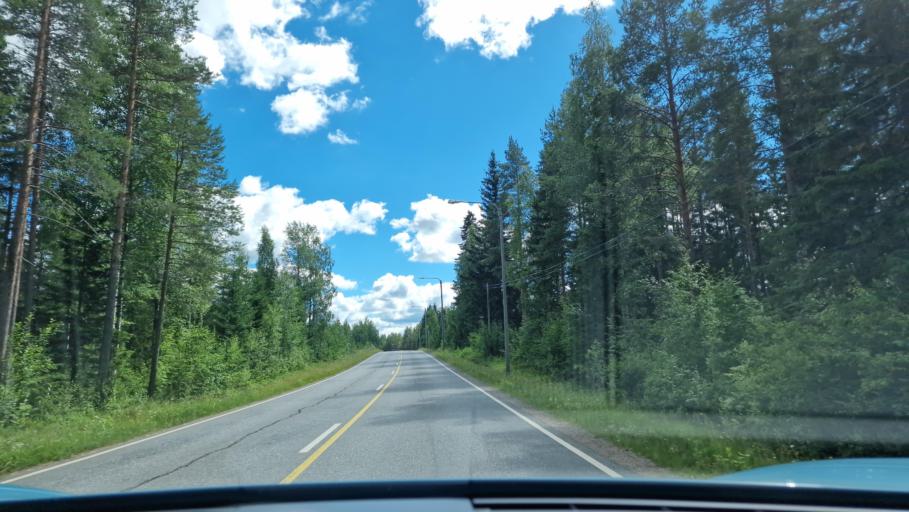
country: FI
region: Southern Ostrobothnia
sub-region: Jaerviseutu
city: Soini
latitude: 62.8387
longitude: 24.3298
